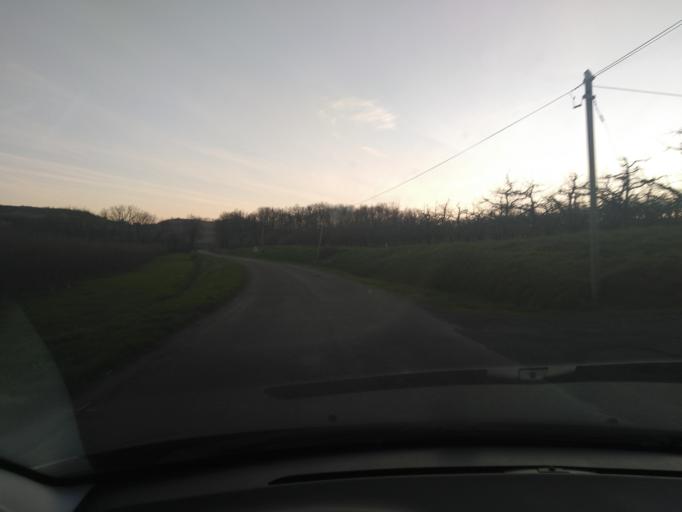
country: FR
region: Aquitaine
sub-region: Departement du Lot-et-Garonne
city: Saint-Hilaire
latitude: 44.5344
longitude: 0.6943
